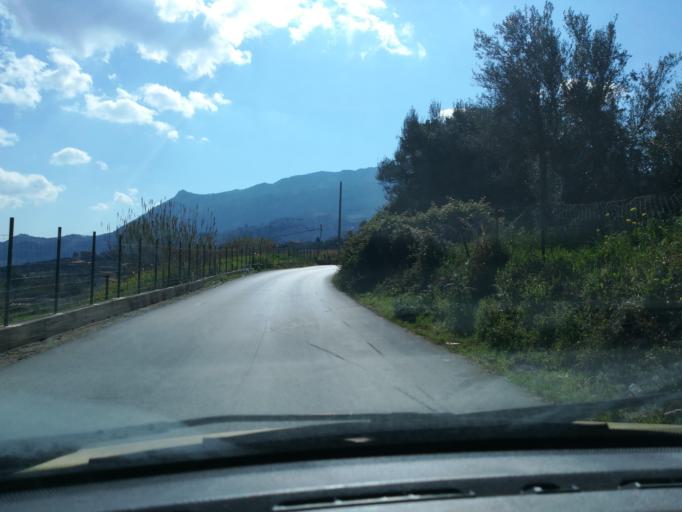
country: IT
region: Sicily
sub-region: Palermo
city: Cannizzaro-Favara
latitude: 38.0504
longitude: 13.2601
